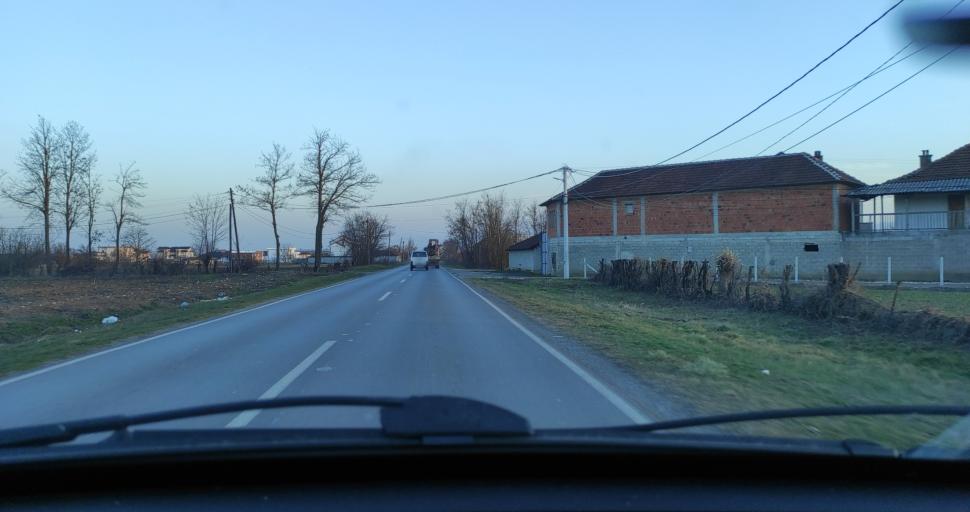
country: XK
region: Gjakova
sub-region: Komuna e Gjakoves
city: Gjakove
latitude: 42.4222
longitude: 20.3926
